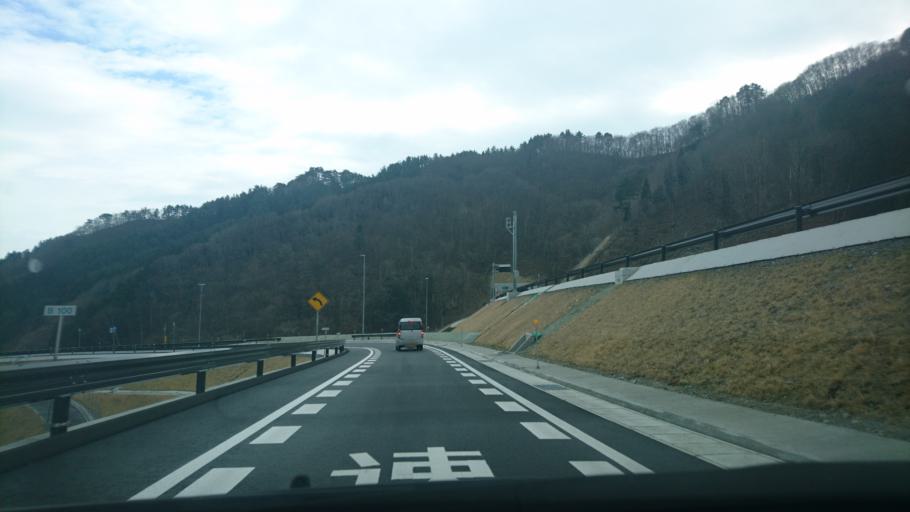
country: JP
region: Iwate
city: Kamaishi
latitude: 39.2190
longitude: 141.8673
